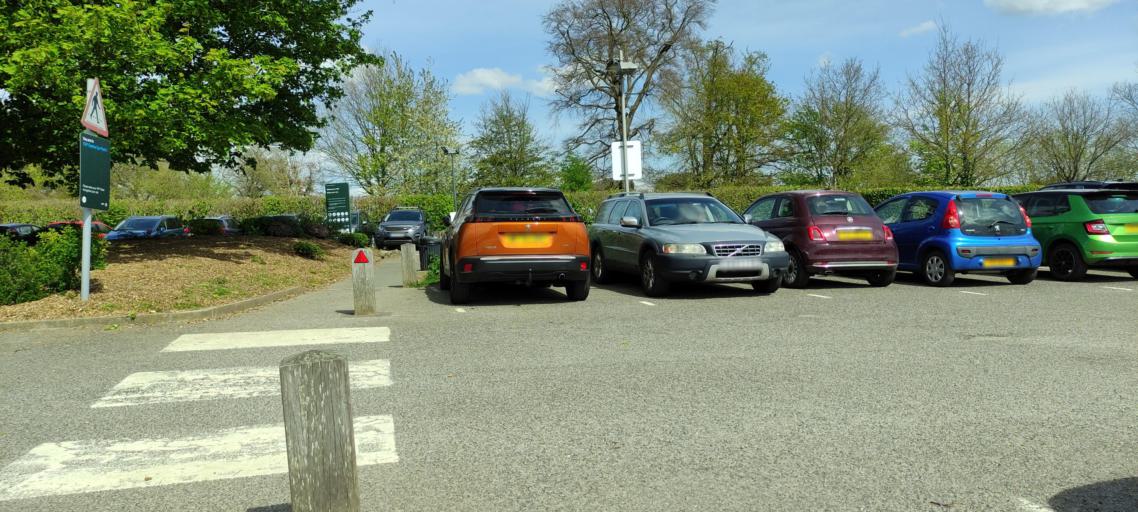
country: GB
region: England
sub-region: Kirklees
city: Clayton West
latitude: 53.6140
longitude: -1.5684
